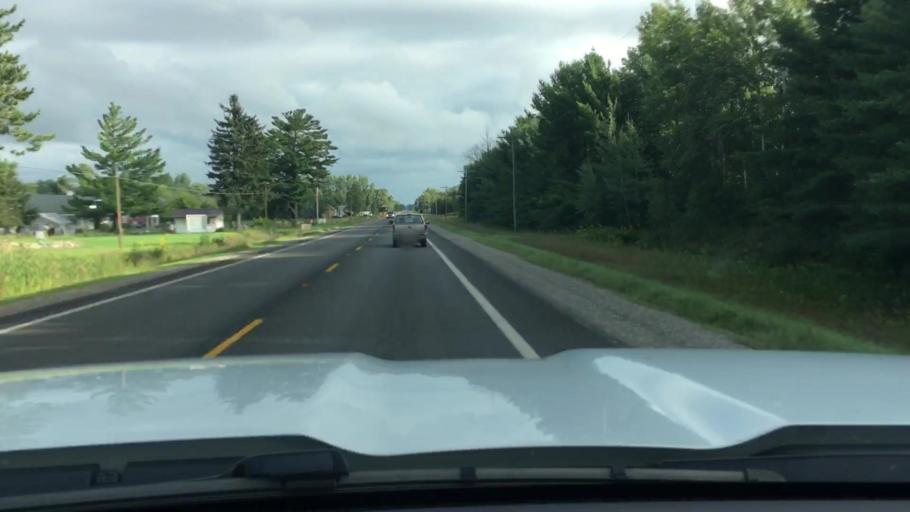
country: US
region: Michigan
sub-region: Tuscola County
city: Caro
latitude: 43.4343
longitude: -83.3849
